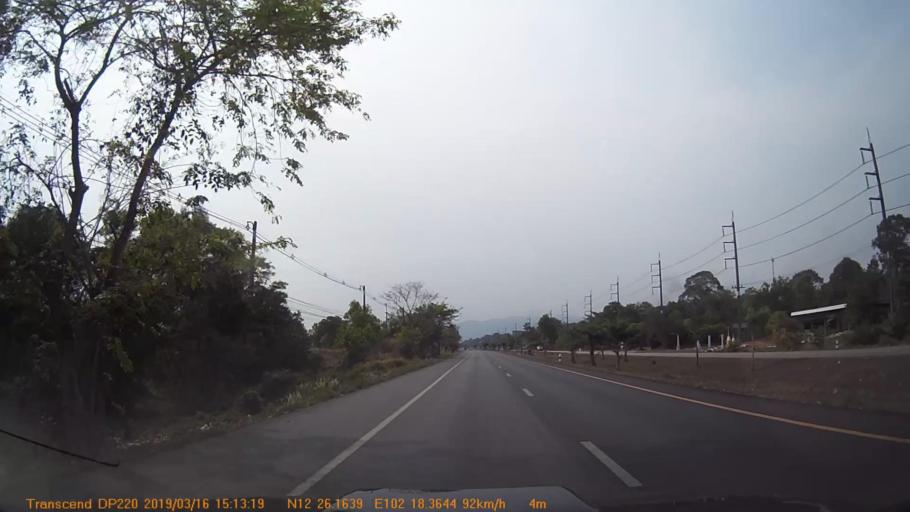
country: TH
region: Chanthaburi
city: Khlung
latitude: 12.4363
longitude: 102.3058
